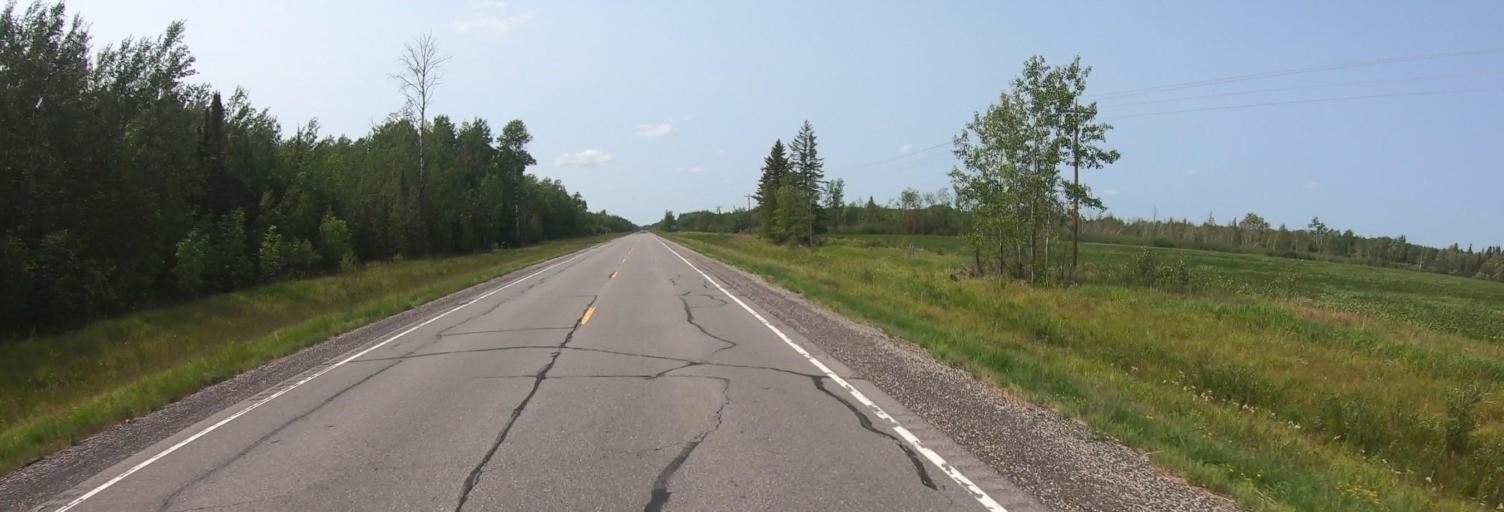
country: US
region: Minnesota
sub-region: Lake of the Woods County
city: Baudette
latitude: 48.6996
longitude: -94.3763
